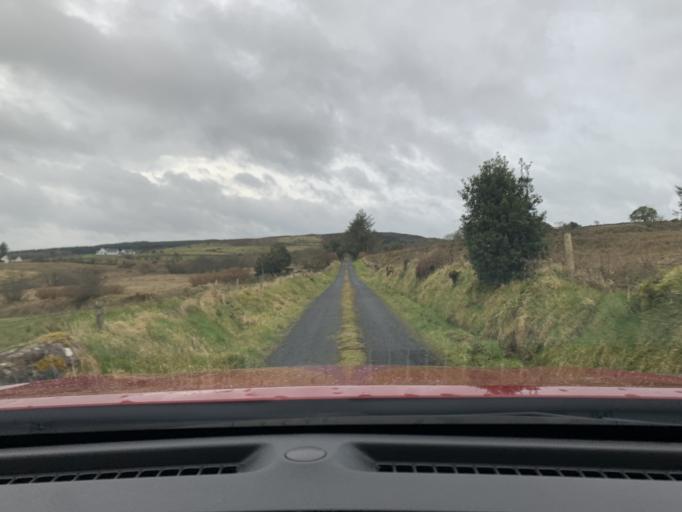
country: IE
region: Connaught
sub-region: Roscommon
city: Ballaghaderreen
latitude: 53.9632
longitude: -8.4988
